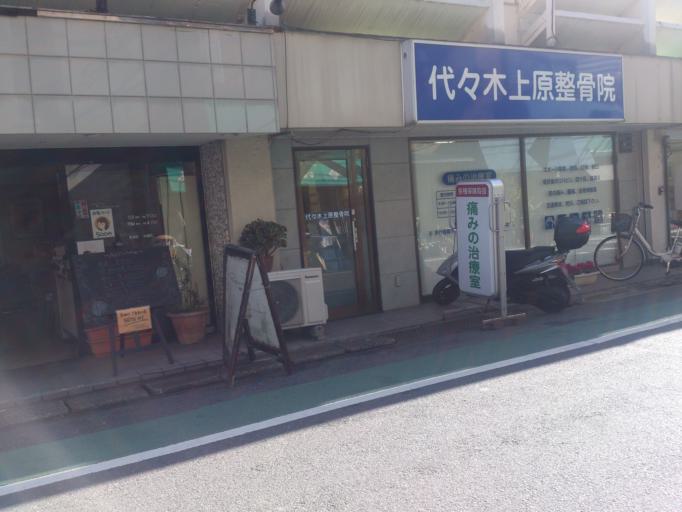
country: JP
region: Tokyo
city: Tokyo
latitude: 35.6686
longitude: 139.6825
